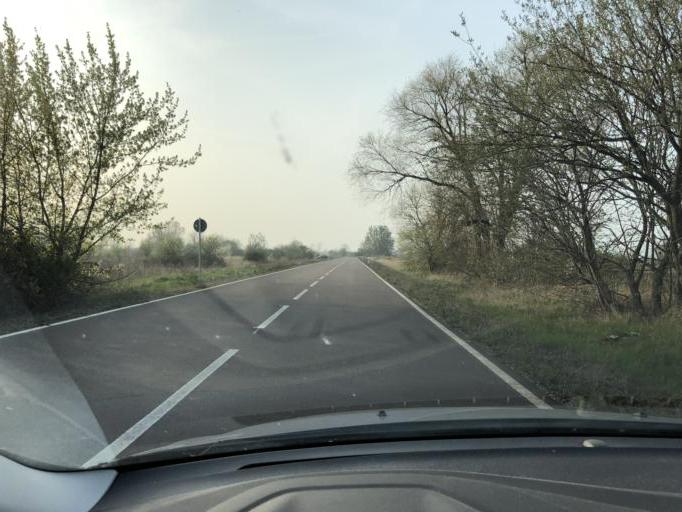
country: DE
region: Saxony
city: Dobernitz
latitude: 51.4971
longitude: 12.3209
